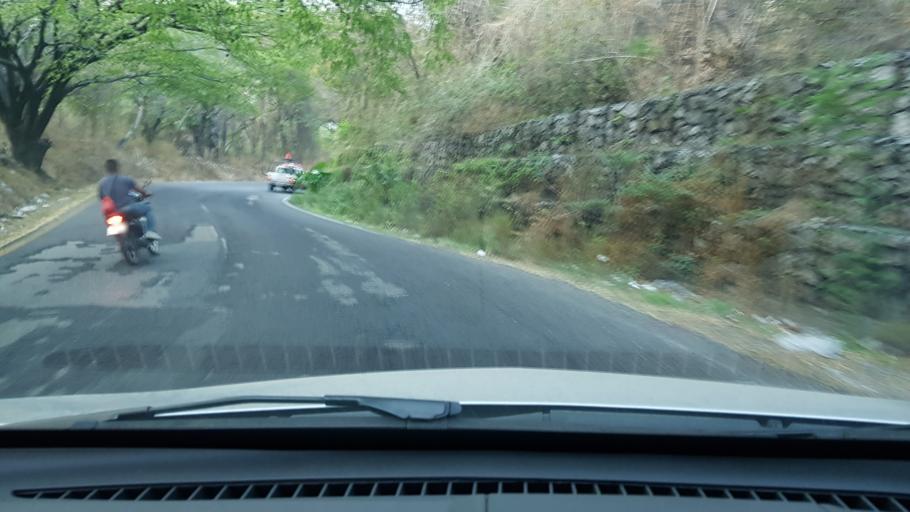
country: MX
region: Morelos
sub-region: Jiutepec
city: Independencia
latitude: 18.8765
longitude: -99.1205
